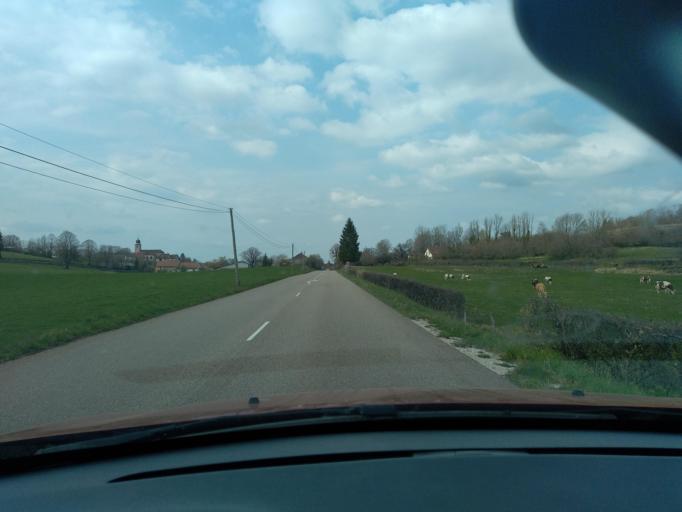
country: FR
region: Franche-Comte
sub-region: Departement du Jura
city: Clairvaux-les-Lacs
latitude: 46.5370
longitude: 5.7539
